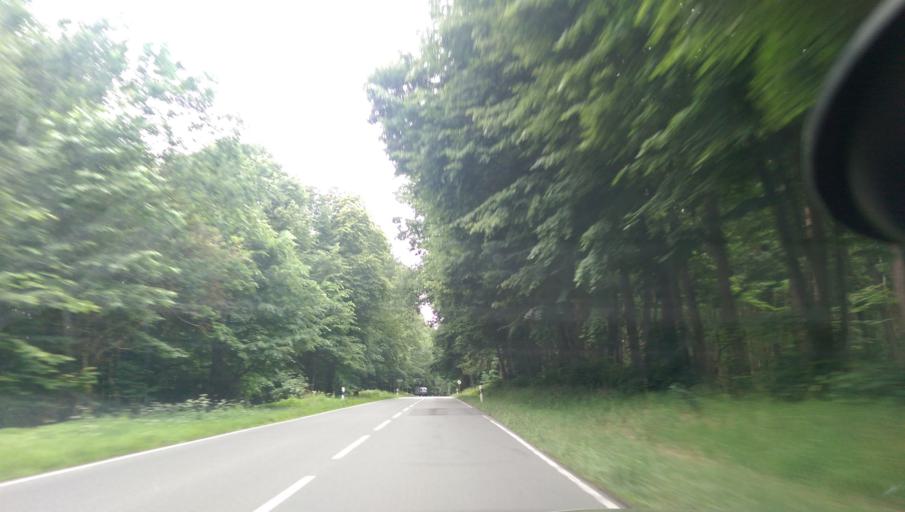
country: DE
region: Lower Saxony
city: Bomlitz
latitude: 52.9562
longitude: 9.6534
